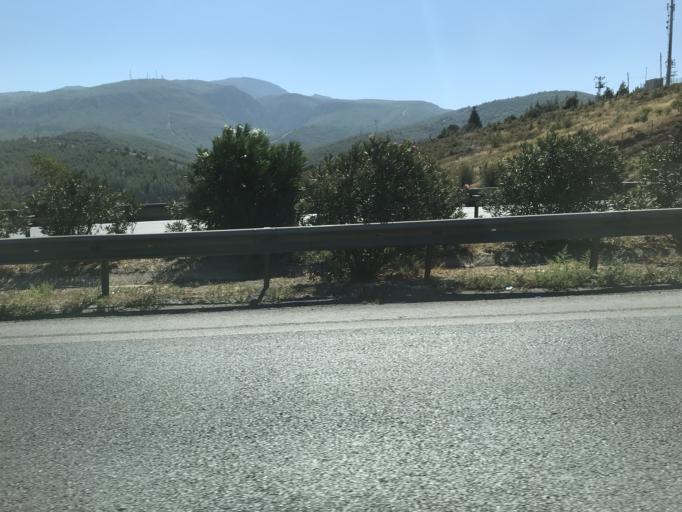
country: TR
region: Izmir
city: Buca
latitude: 38.4015
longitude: 27.2300
